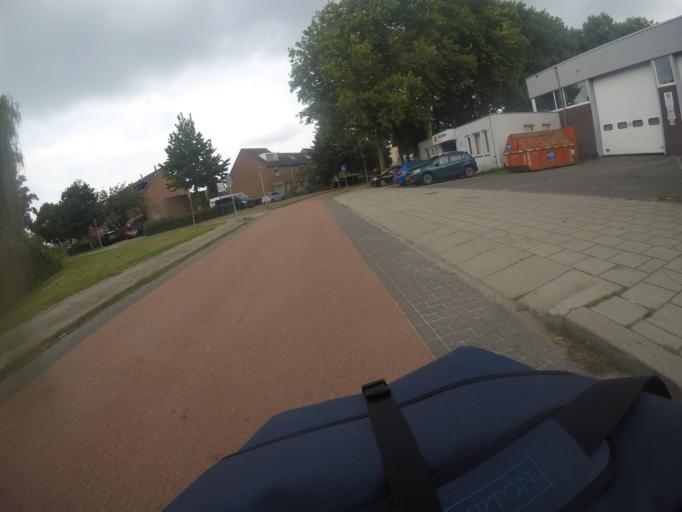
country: NL
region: Flevoland
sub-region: Gemeente Almere
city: Almere Stad
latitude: 52.3456
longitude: 5.2185
